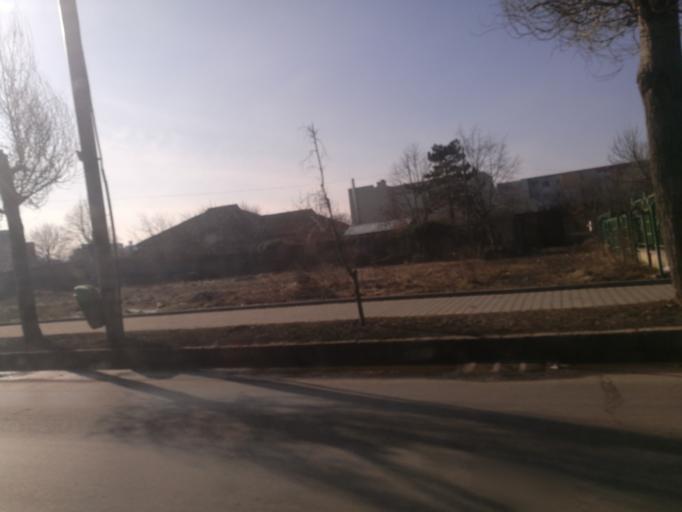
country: RO
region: Iasi
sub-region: Municipiul Iasi
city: Iasi
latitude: 47.1486
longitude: 27.5798
